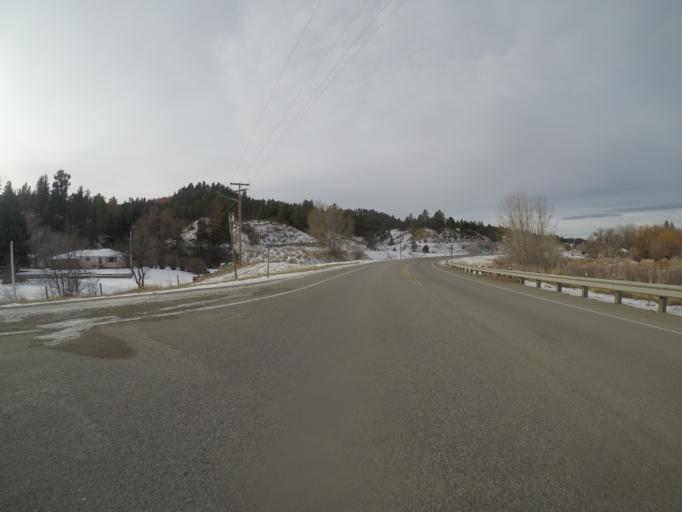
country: US
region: Montana
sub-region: Stillwater County
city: Columbus
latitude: 45.6275
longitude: -109.2578
